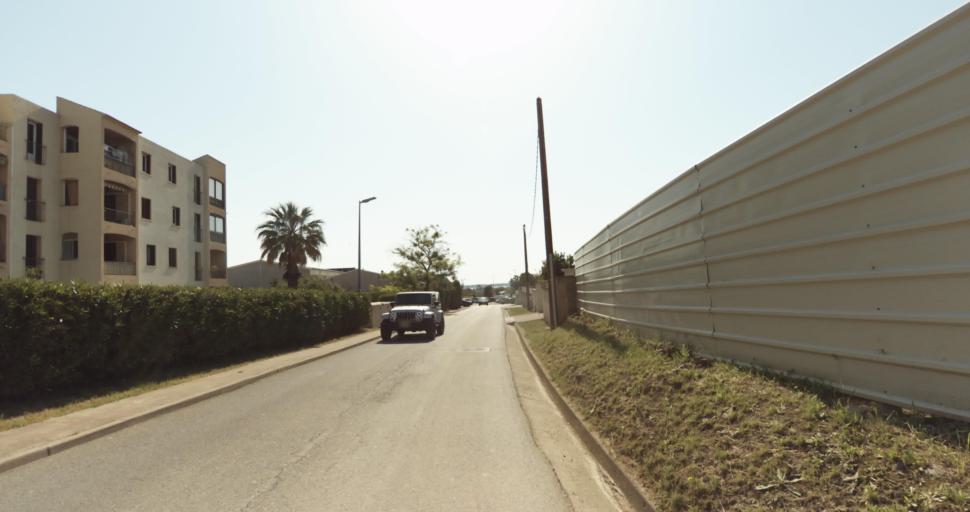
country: FR
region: Corsica
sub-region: Departement de la Haute-Corse
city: Biguglia
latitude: 42.6203
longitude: 9.4351
